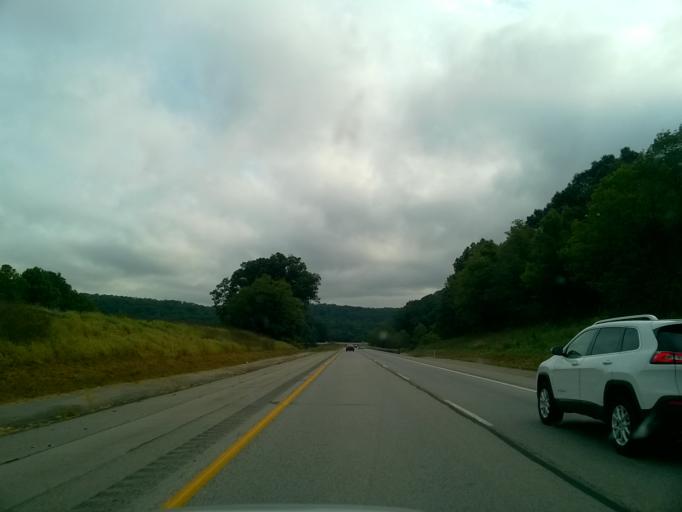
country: US
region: Indiana
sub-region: Crawford County
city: English
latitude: 38.2494
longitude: -86.3394
